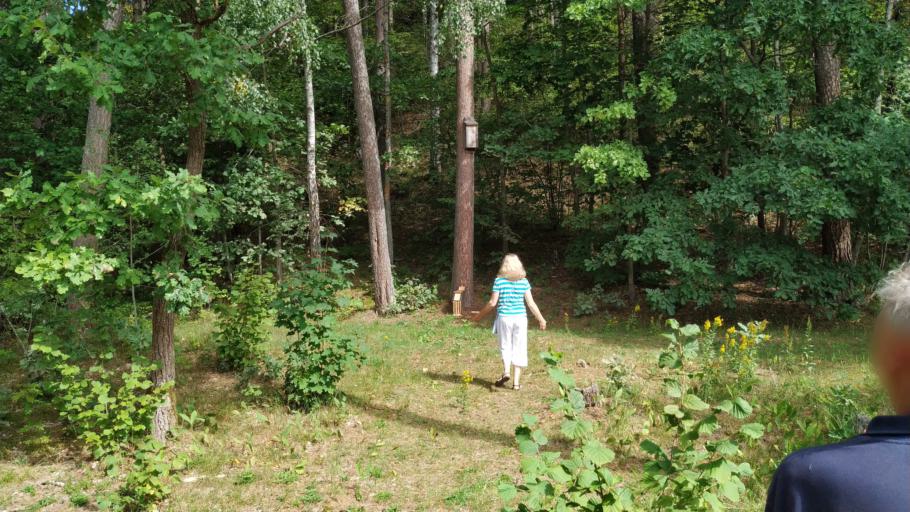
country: LT
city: Grigiskes
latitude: 54.8065
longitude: 24.9691
